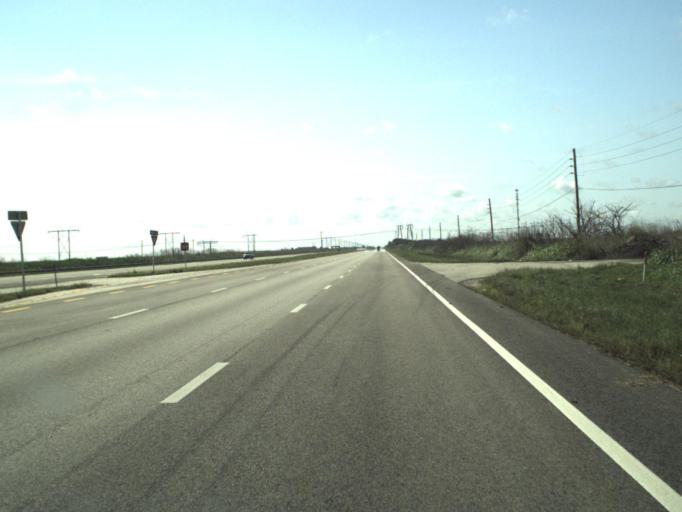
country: US
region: Florida
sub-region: Broward County
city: Coral Springs
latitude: 26.3490
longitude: -80.5490
